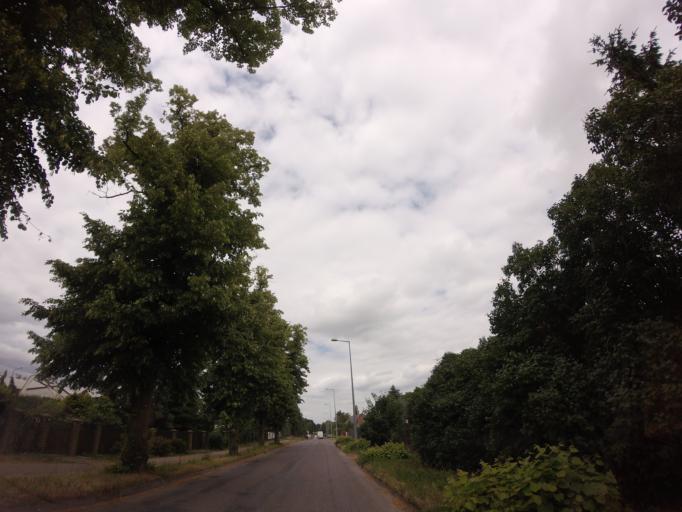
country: PL
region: Lubusz
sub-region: Powiat strzelecko-drezdenecki
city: Strzelce Krajenskie
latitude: 52.8795
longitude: 15.5443
